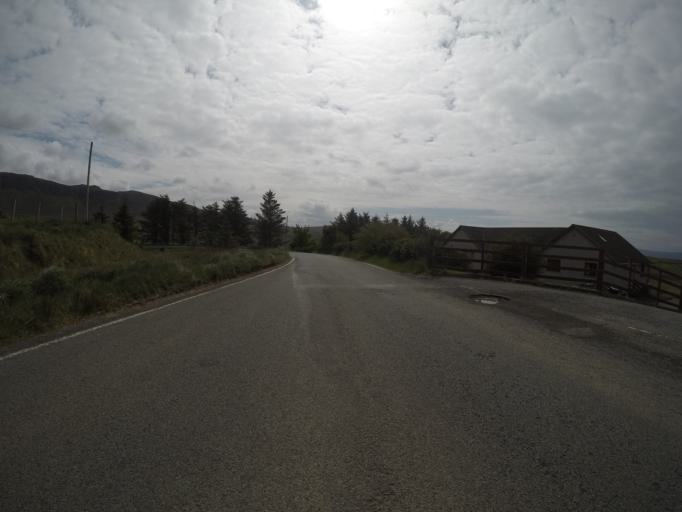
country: GB
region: Scotland
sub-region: Highland
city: Portree
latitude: 57.6223
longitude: -6.3776
